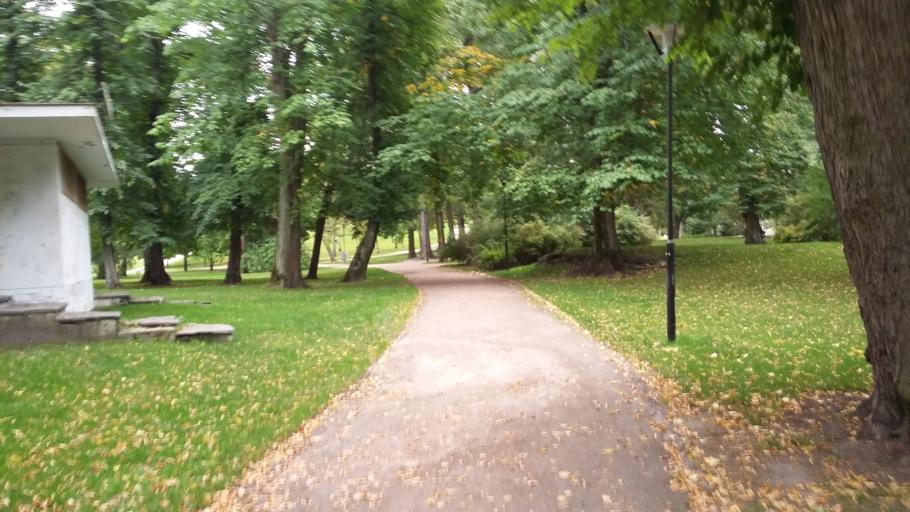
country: FI
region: Uusimaa
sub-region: Helsinki
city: Helsinki
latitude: 60.1577
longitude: 24.9551
